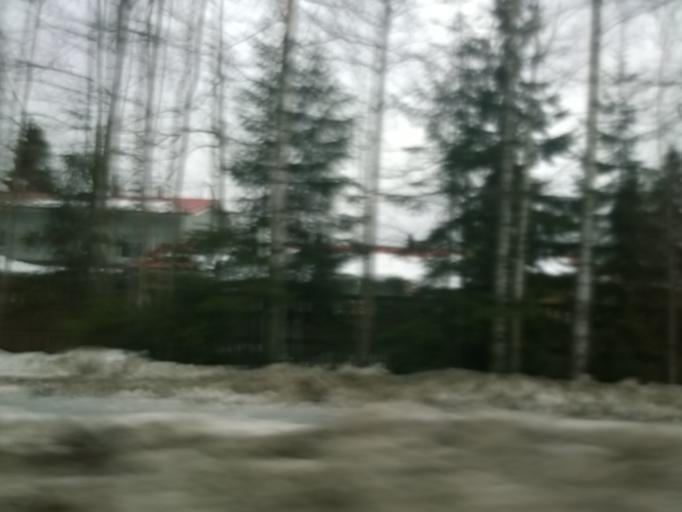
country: FI
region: Pirkanmaa
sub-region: Tampere
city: Tampere
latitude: 61.4147
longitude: 23.7602
